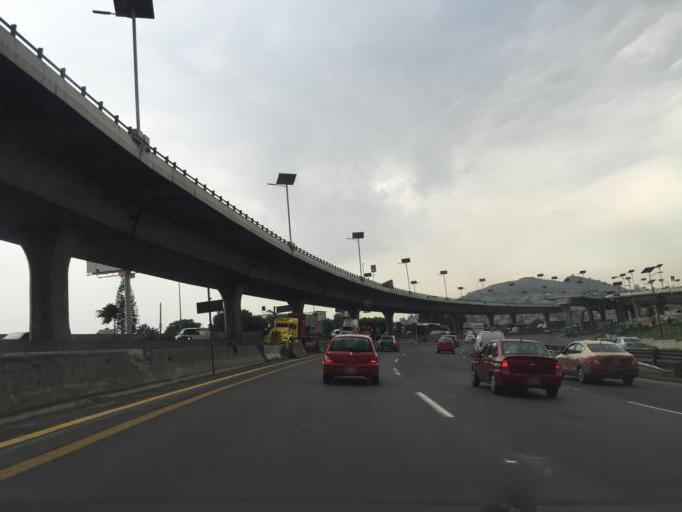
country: MX
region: Mexico
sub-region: Tultitlan
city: Buenavista
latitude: 19.6007
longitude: -99.1889
